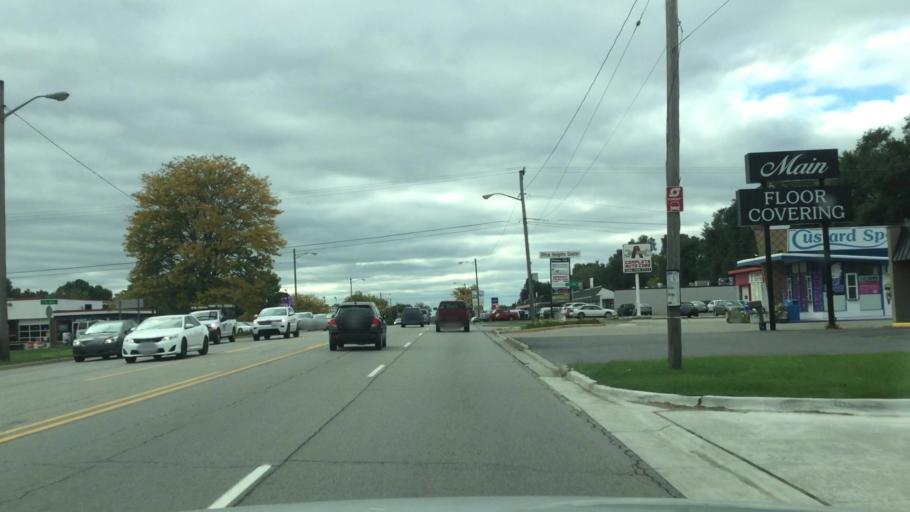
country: US
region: Michigan
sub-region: Macomb County
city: Utica
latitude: 42.6401
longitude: -83.0330
